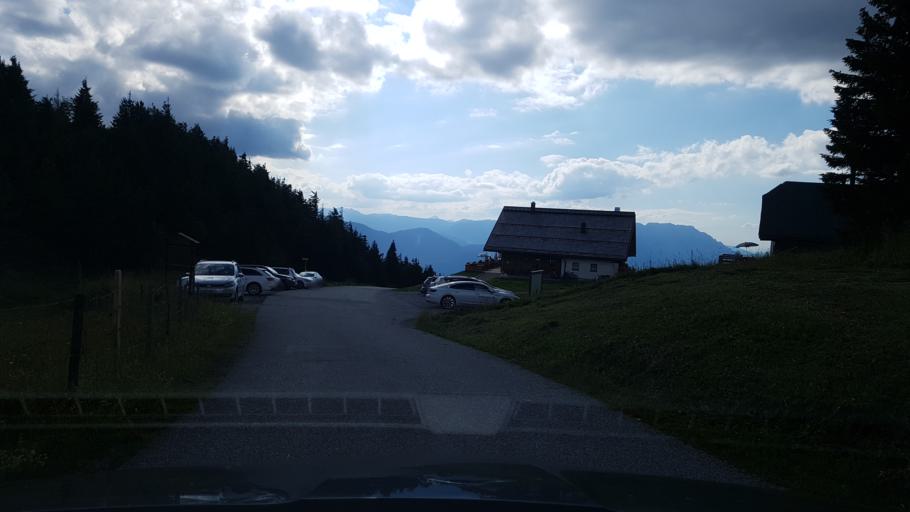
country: AT
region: Salzburg
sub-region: Politischer Bezirk Hallein
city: Scheffau am Tennengebirge
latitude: 47.6357
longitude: 13.2619
